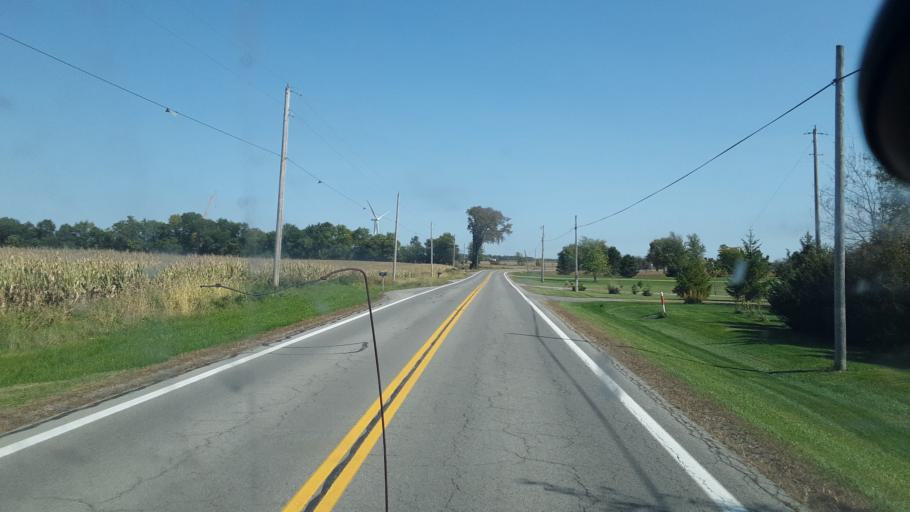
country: US
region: Ohio
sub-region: Logan County
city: Northwood
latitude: 40.5048
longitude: -83.7230
